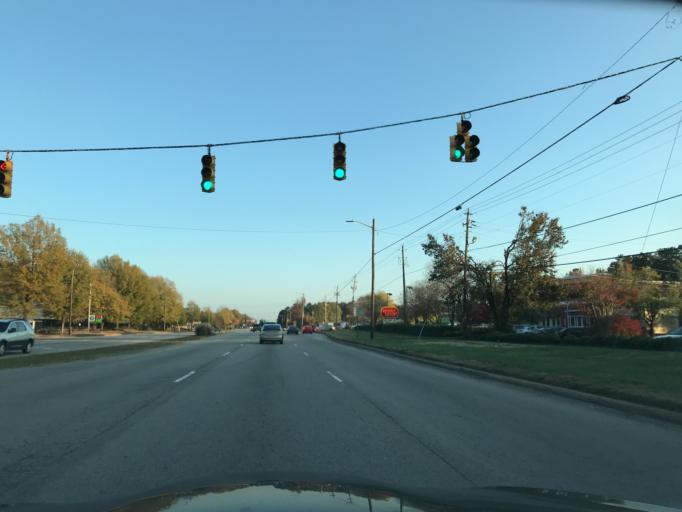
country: US
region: North Carolina
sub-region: Wake County
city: West Raleigh
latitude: 35.8568
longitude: -78.7037
